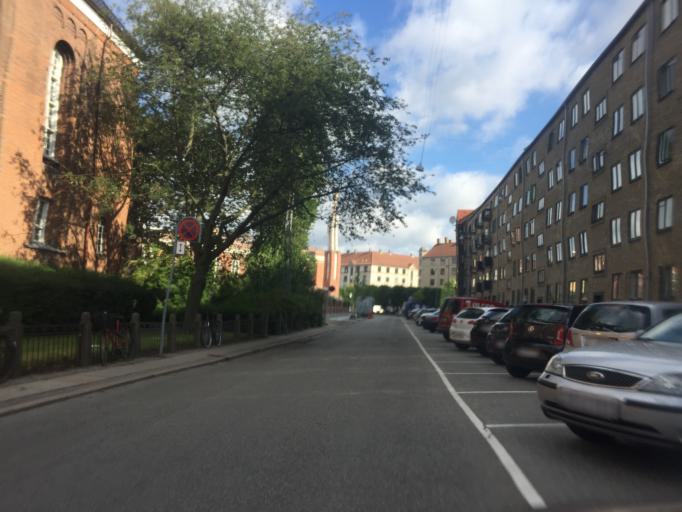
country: DK
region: Capital Region
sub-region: Frederiksberg Kommune
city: Frederiksberg
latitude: 55.6919
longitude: 12.5349
